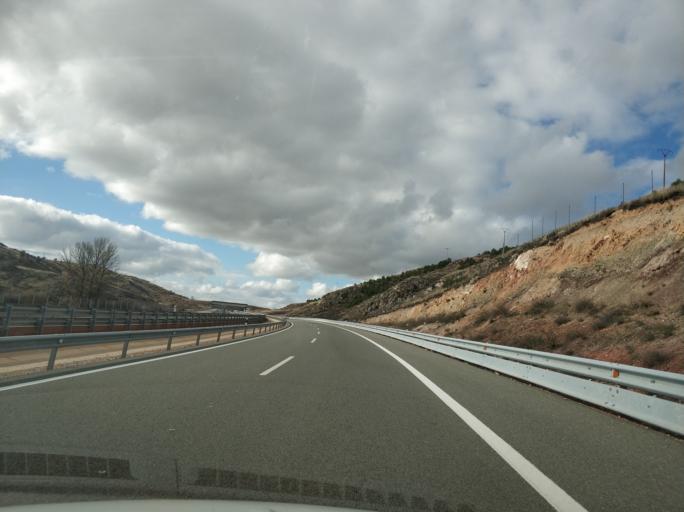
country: ES
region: Castille and Leon
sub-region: Provincia de Soria
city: Medinaceli
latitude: 41.1936
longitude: -2.4374
